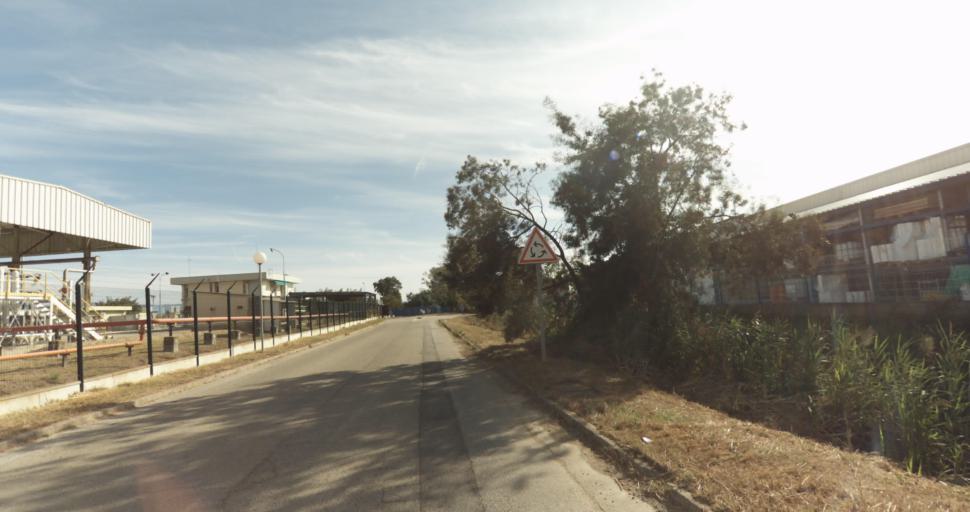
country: FR
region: Corsica
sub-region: Departement de la Corse-du-Sud
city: Afa
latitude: 41.9301
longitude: 8.7906
